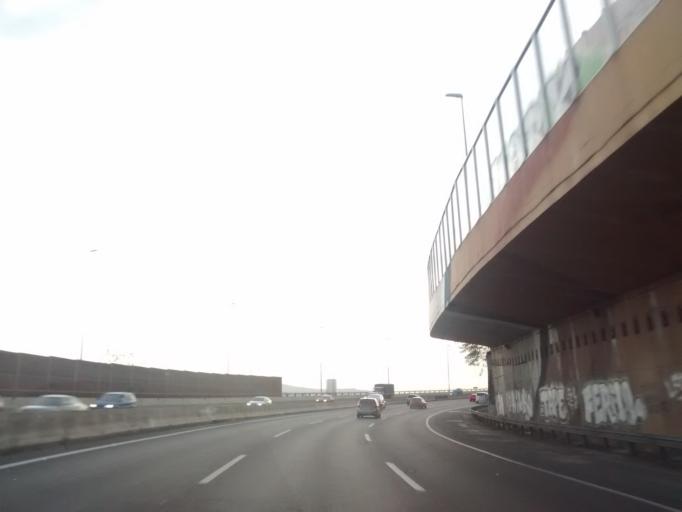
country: ES
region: Basque Country
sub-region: Bizkaia
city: Barakaldo
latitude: 43.2744
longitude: -2.9711
